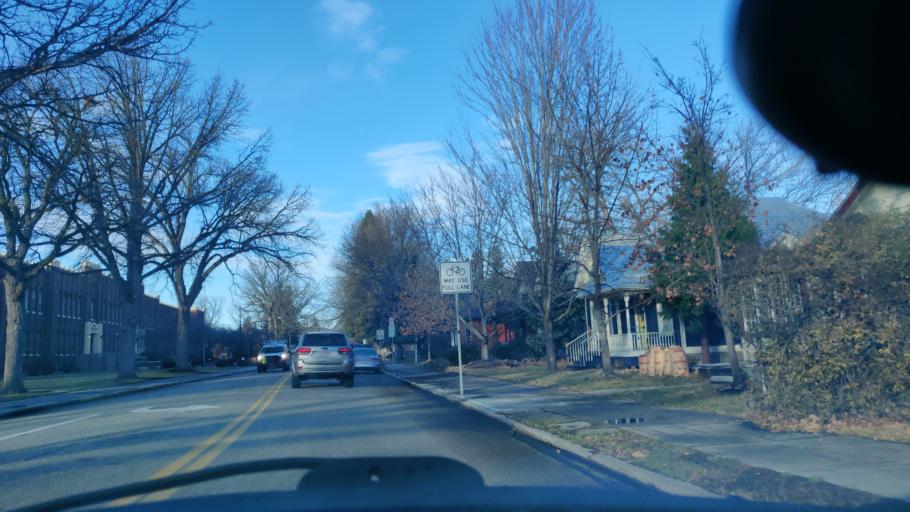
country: US
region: Idaho
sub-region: Ada County
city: Boise
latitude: 43.6250
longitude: -116.2033
